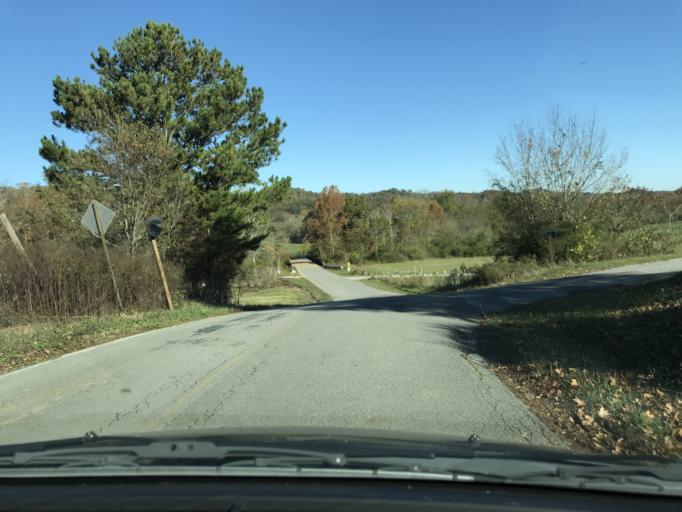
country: US
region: Georgia
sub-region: Dade County
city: Trenton
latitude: 34.8954
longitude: -85.4635
